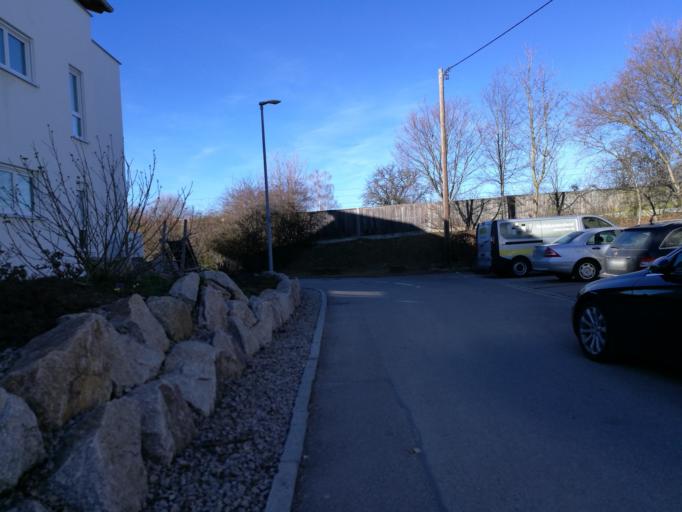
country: DE
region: Baden-Wuerttemberg
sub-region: Regierungsbezirk Stuttgart
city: Leinfelden-Echterdingen
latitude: 48.6927
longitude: 9.1473
